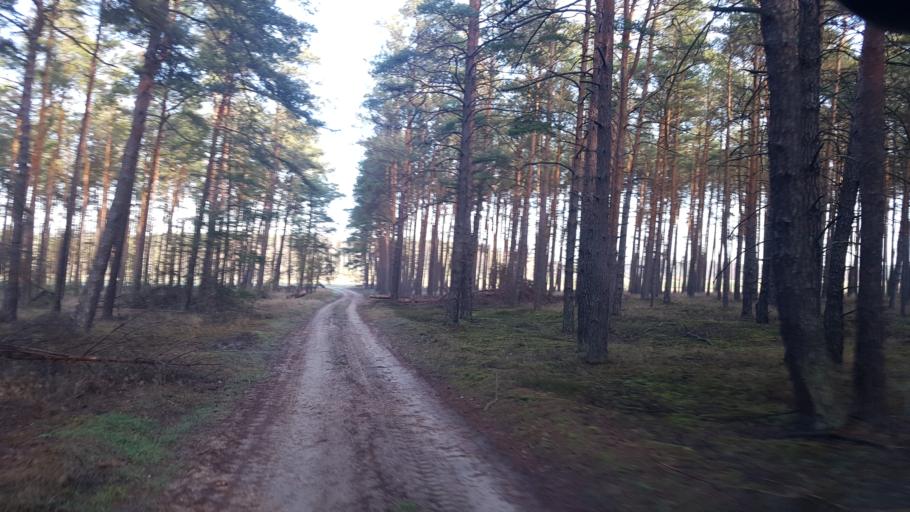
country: DE
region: Brandenburg
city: Schilda
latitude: 51.6363
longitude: 13.3973
